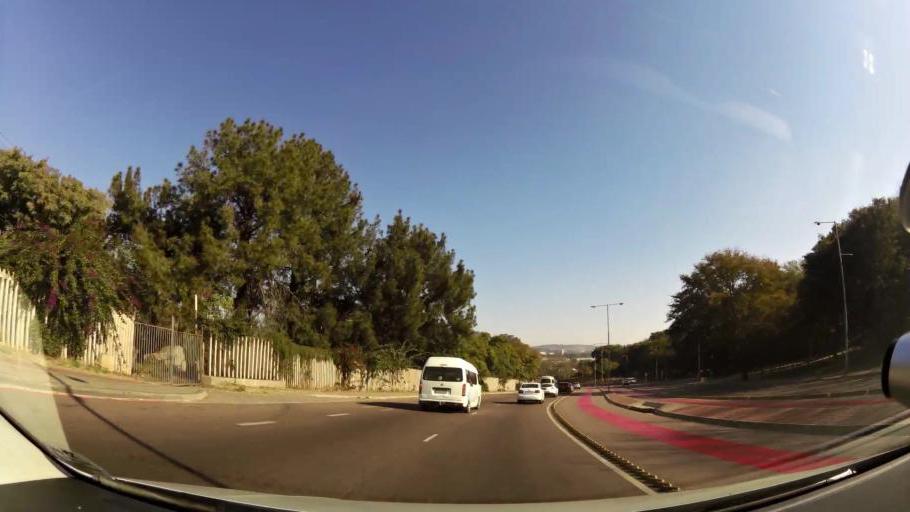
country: ZA
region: Gauteng
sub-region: City of Tshwane Metropolitan Municipality
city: Pretoria
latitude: -25.7327
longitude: 28.1893
